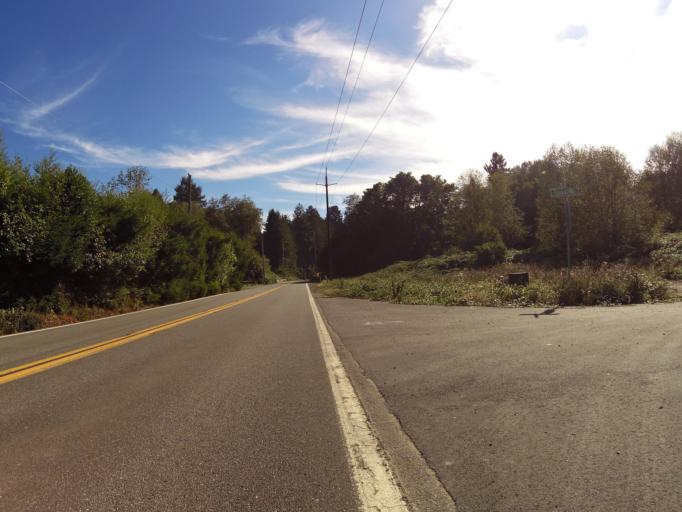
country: US
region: California
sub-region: Del Norte County
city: Bertsch-Oceanview
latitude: 41.8601
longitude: -124.1178
